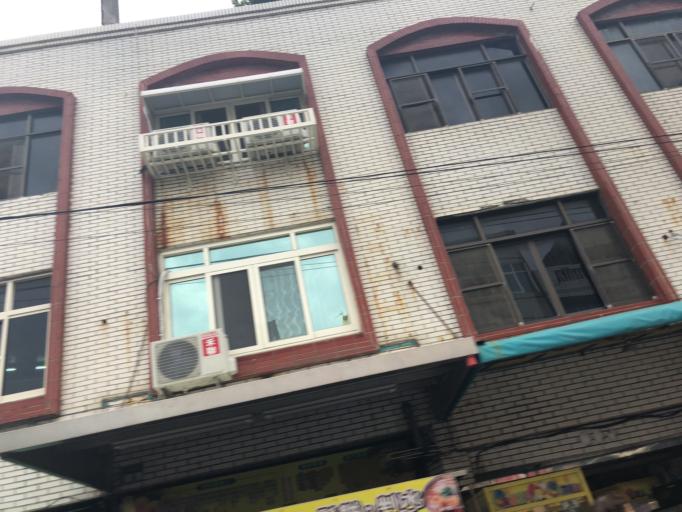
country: TW
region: Taiwan
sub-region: Chiayi
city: Taibao
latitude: 23.7001
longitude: 120.1989
